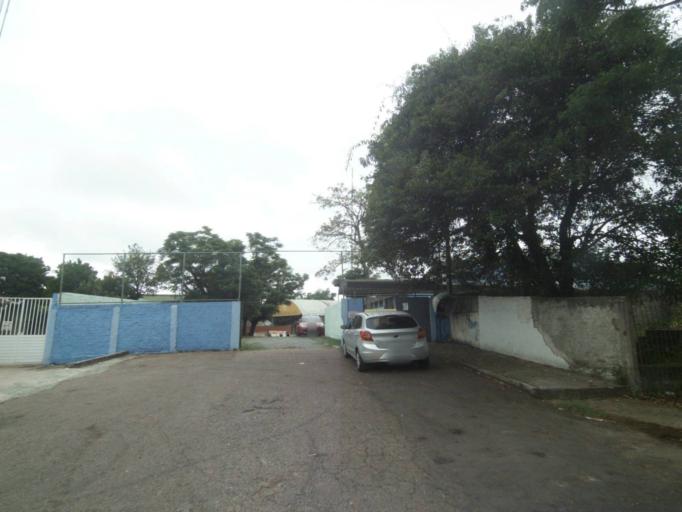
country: BR
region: Parana
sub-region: Sao Jose Dos Pinhais
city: Sao Jose dos Pinhais
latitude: -25.5443
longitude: -49.2761
